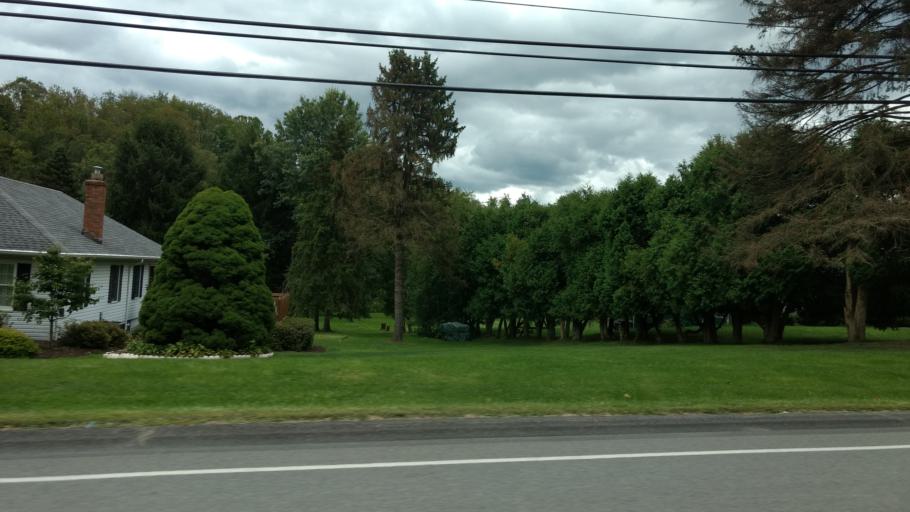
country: US
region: Pennsylvania
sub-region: Westmoreland County
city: Lynnwood-Pricedale
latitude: 40.1517
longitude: -79.8325
